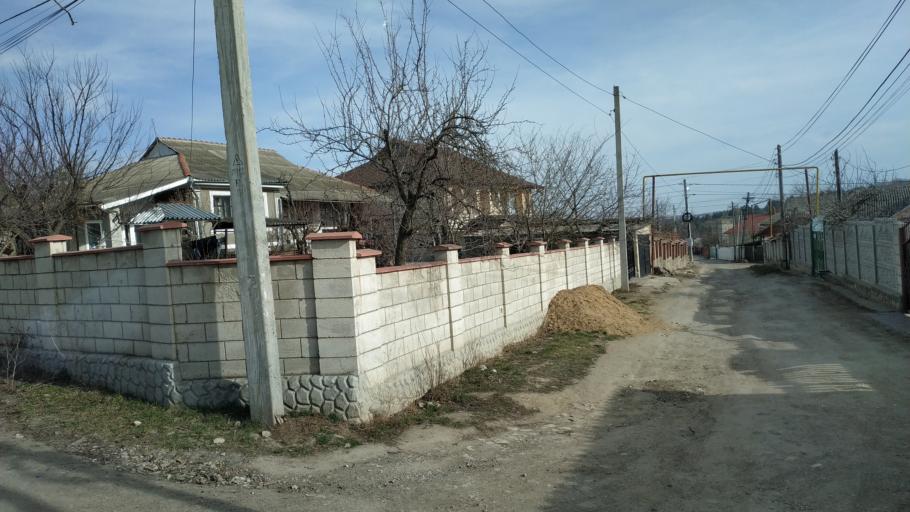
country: MD
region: Chisinau
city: Vatra
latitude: 47.0745
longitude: 28.6831
